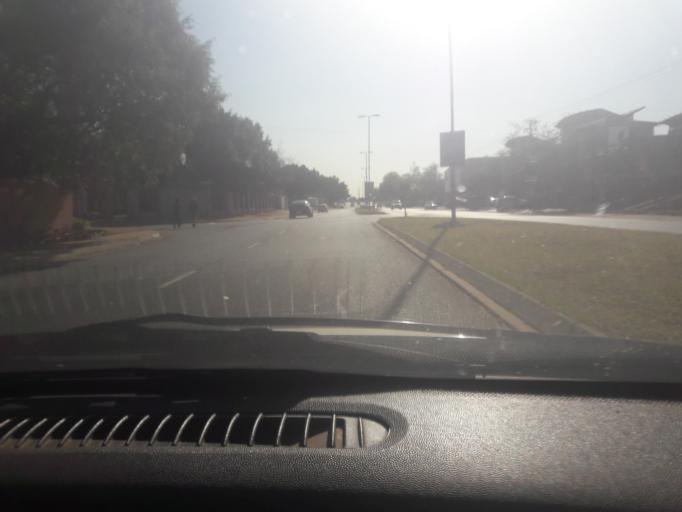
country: ZA
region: Gauteng
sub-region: City of Tshwane Metropolitan Municipality
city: Pretoria
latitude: -25.7720
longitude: 28.2648
